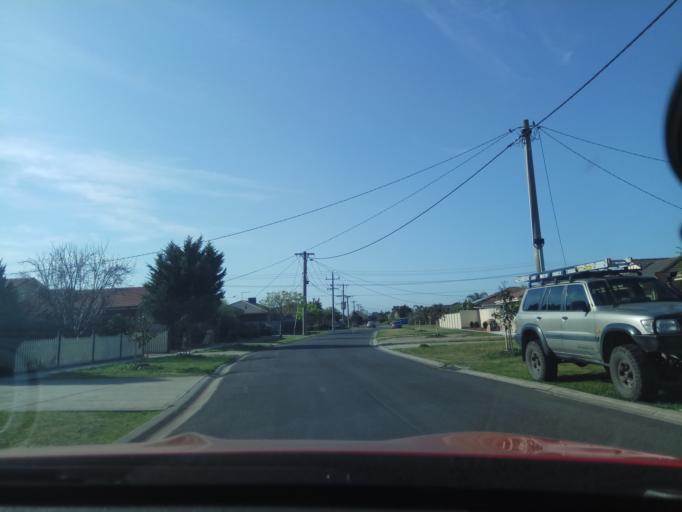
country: AU
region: Victoria
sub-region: Hobsons Bay
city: Altona Meadows
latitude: -37.8773
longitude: 144.7711
